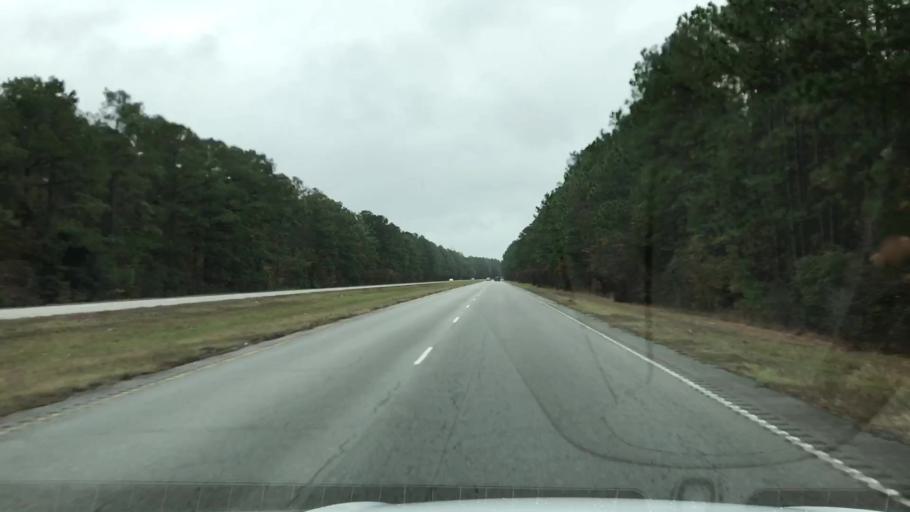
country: US
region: South Carolina
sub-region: Charleston County
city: Awendaw
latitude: 32.9673
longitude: -79.6795
